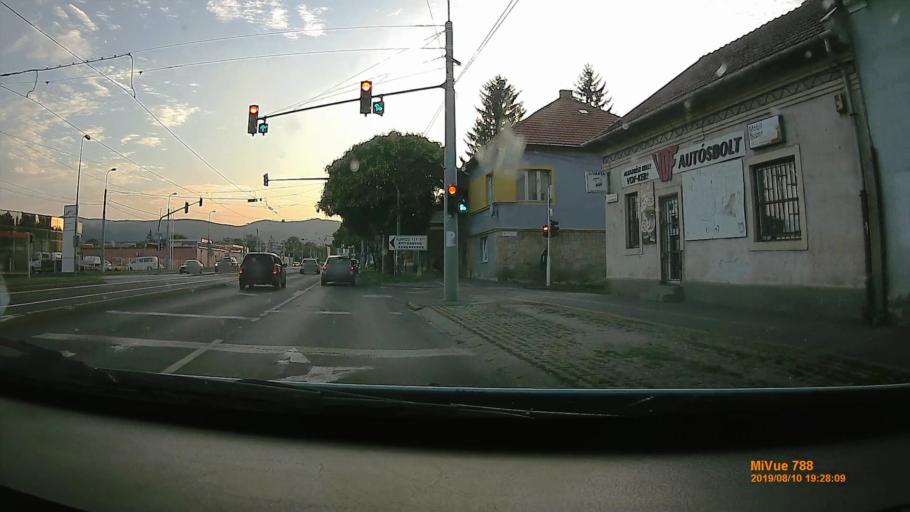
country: HU
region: Borsod-Abauj-Zemplen
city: Miskolc
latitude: 48.1014
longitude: 20.7286
